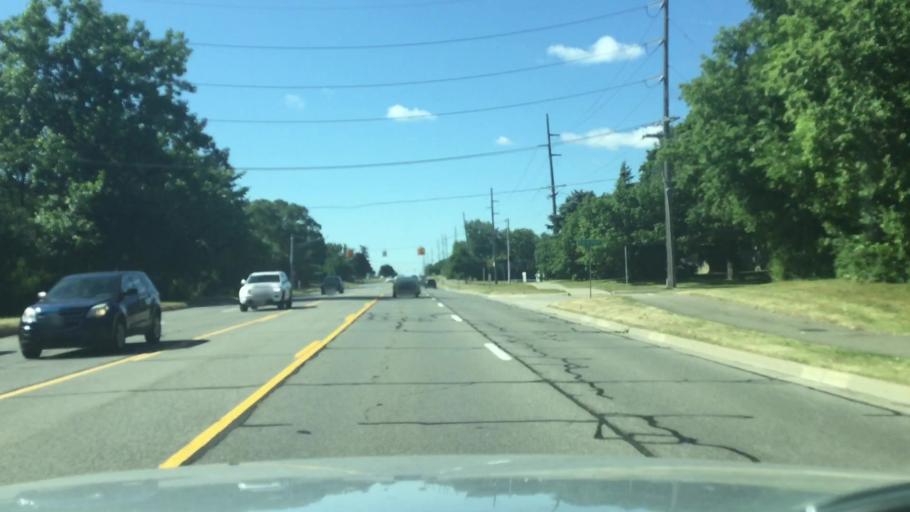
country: US
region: Michigan
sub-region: Oakland County
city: West Bloomfield Township
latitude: 42.5517
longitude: -83.3611
